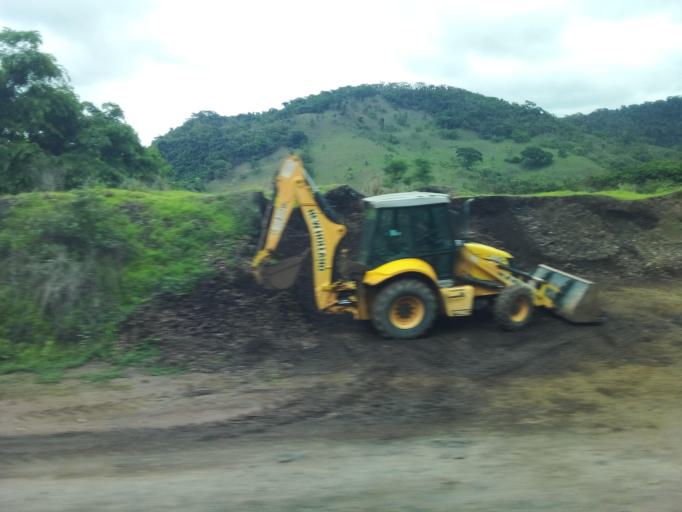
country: BR
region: Minas Gerais
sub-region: Nova Era
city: Nova Era
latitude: -19.6763
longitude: -42.8953
